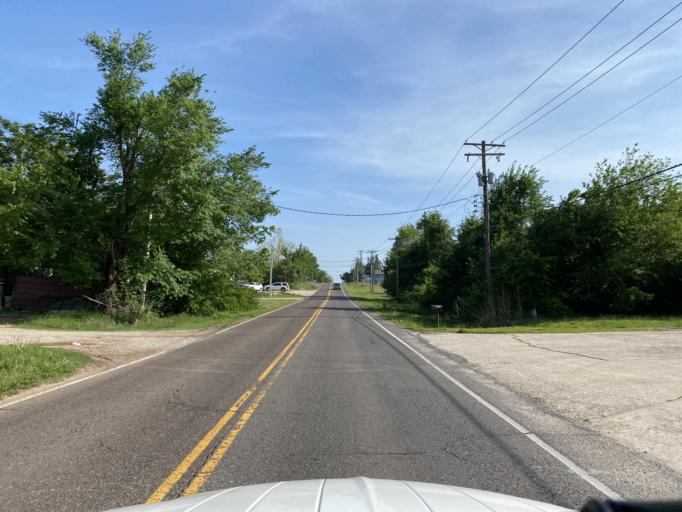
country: US
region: Oklahoma
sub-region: Oklahoma County
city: Nicoma Park
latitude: 35.4917
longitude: -97.3357
